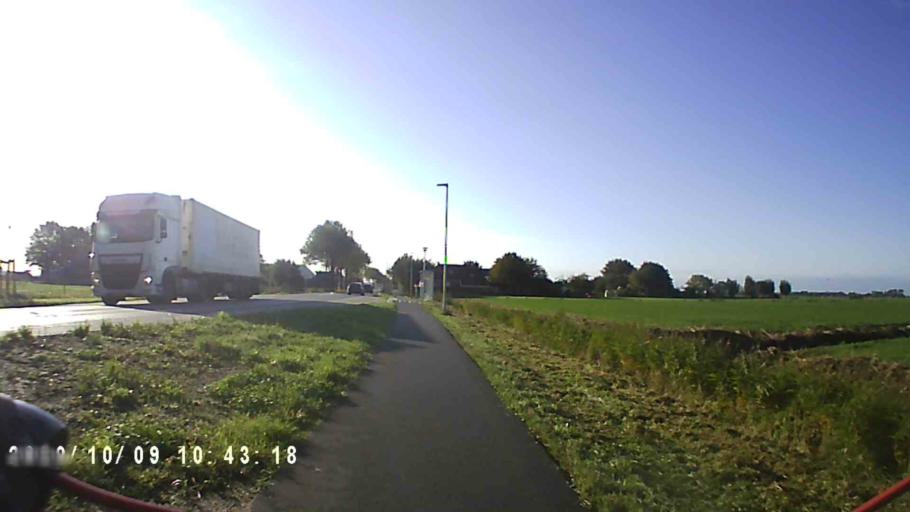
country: NL
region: Groningen
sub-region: Gemeente Groningen
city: Korrewegwijk
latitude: 53.2714
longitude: 6.5359
